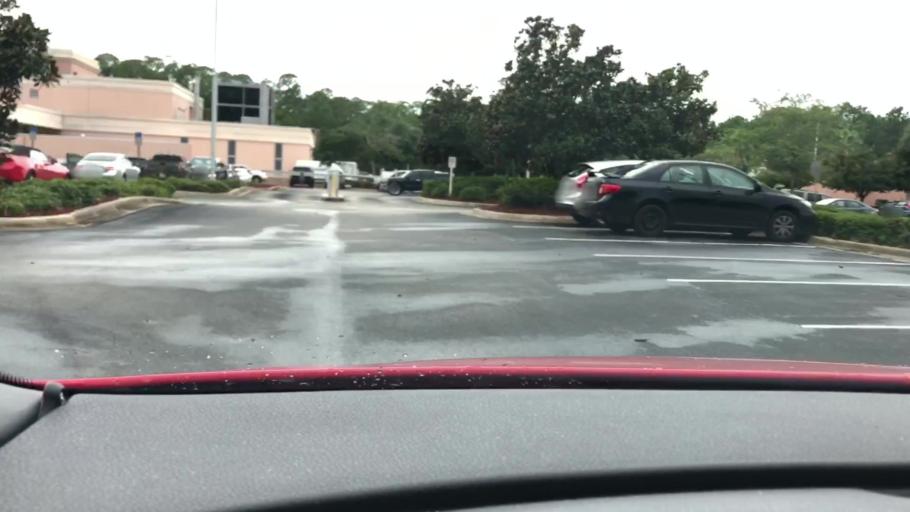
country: US
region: Florida
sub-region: Flagler County
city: Flagler Beach
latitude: 29.4804
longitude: -81.1884
